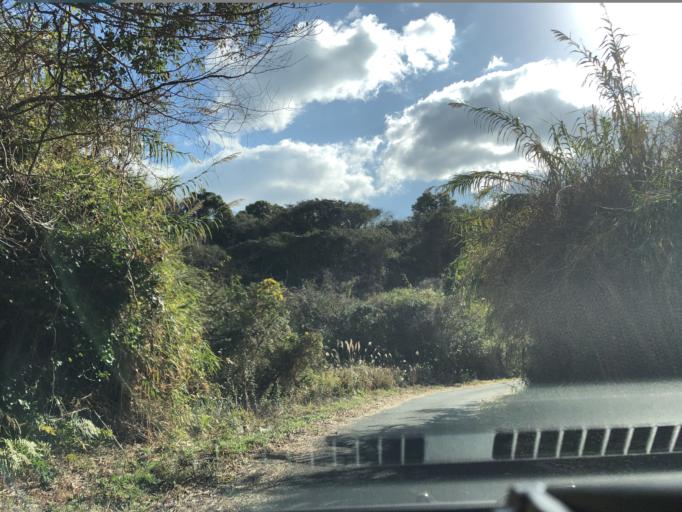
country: JP
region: Kochi
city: Sukumo
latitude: 32.9124
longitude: 132.6943
